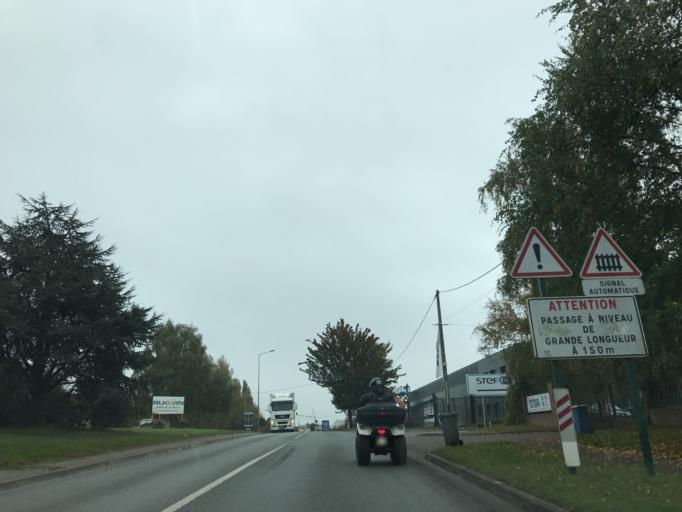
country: FR
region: Nord-Pas-de-Calais
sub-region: Departement du Pas-de-Calais
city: Saint-Laurent-Blangy
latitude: 50.2945
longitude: 2.8049
